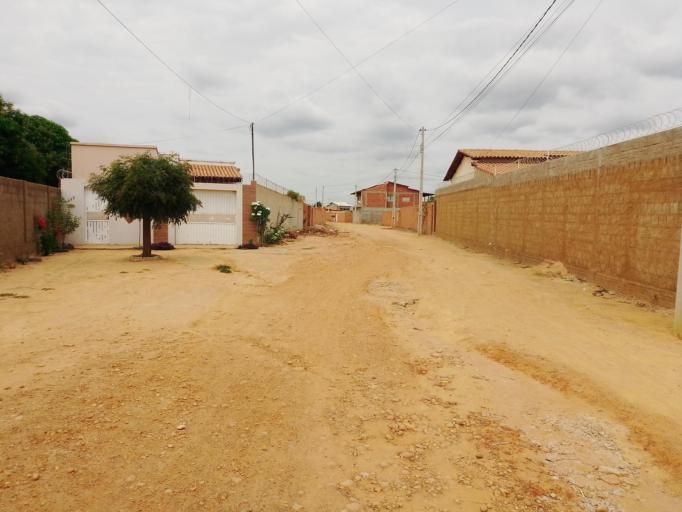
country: BR
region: Minas Gerais
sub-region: Sao Joao Do Paraiso
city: Sao Joao do Paraiso
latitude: -14.9000
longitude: -41.9730
